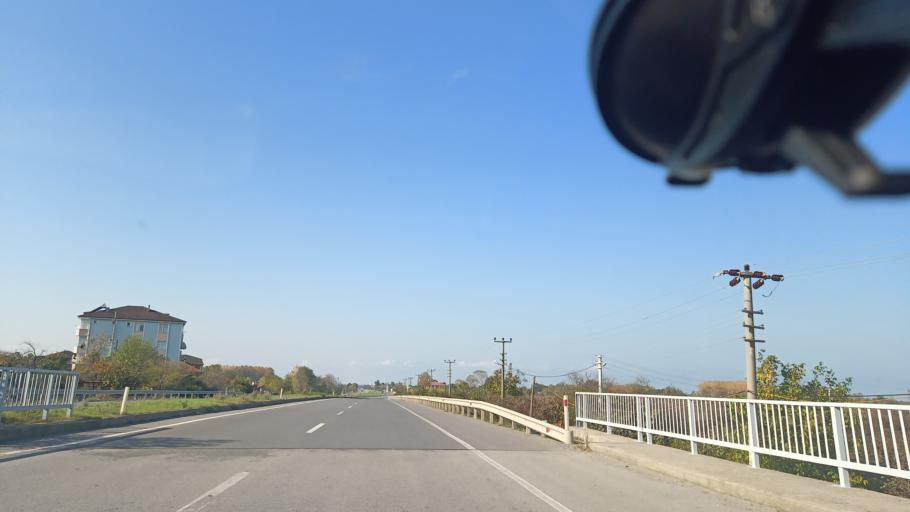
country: TR
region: Sakarya
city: Karasu
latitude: 41.0732
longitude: 30.7883
